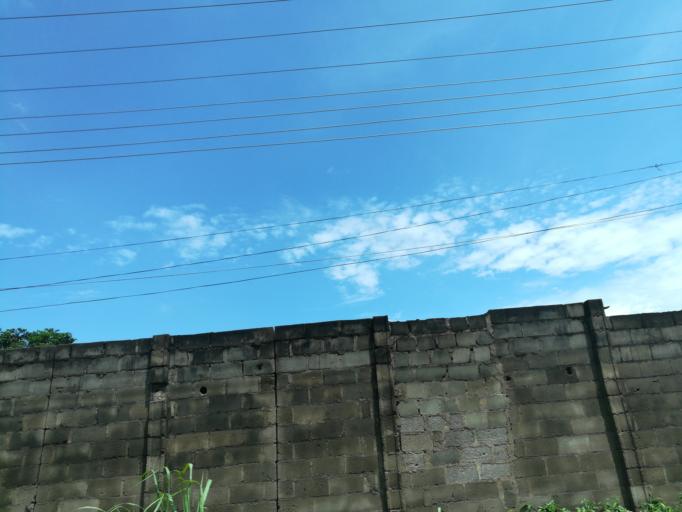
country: NG
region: Lagos
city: Agege
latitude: 6.6057
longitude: 3.3272
